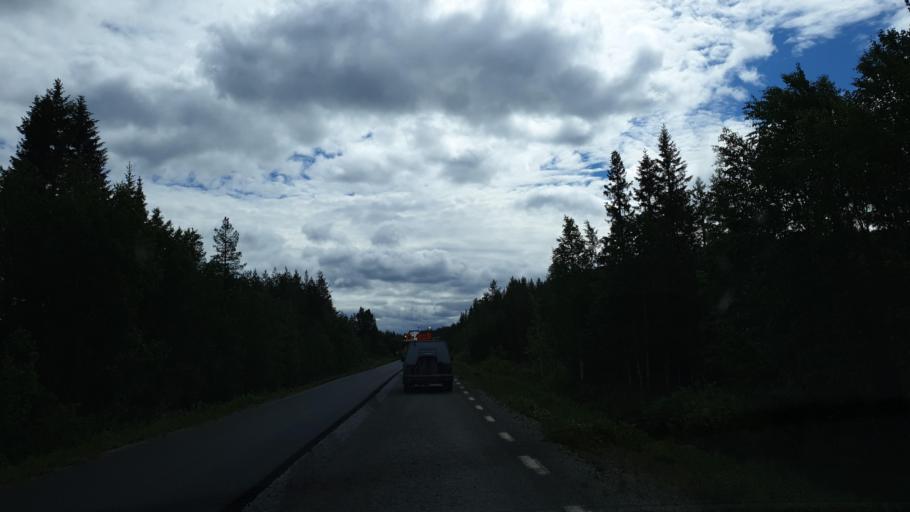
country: SE
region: Vaesterbotten
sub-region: Vilhelmina Kommun
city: Sjoberg
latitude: 64.8941
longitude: 15.8589
